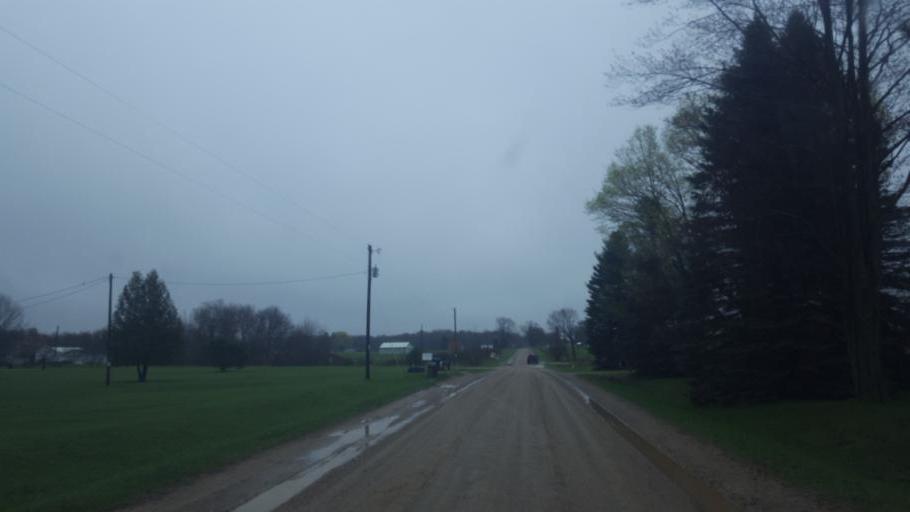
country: US
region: Michigan
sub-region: Isabella County
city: Lake Isabella
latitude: 43.5530
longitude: -84.9734
